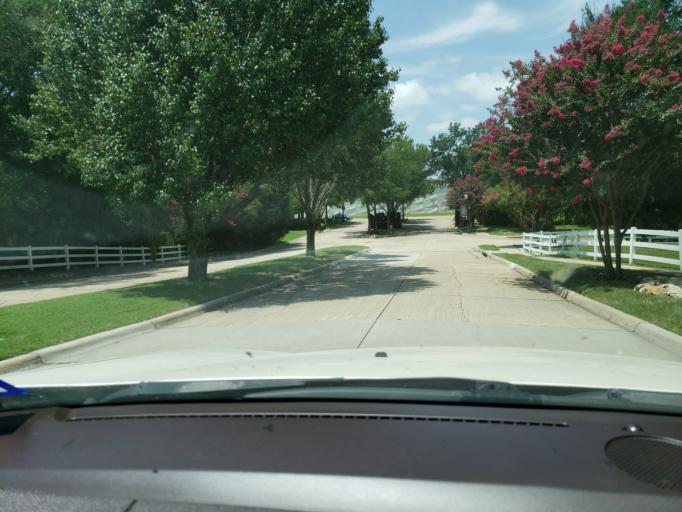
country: US
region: Texas
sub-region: Dallas County
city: Rowlett
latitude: 32.8935
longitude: -96.5544
